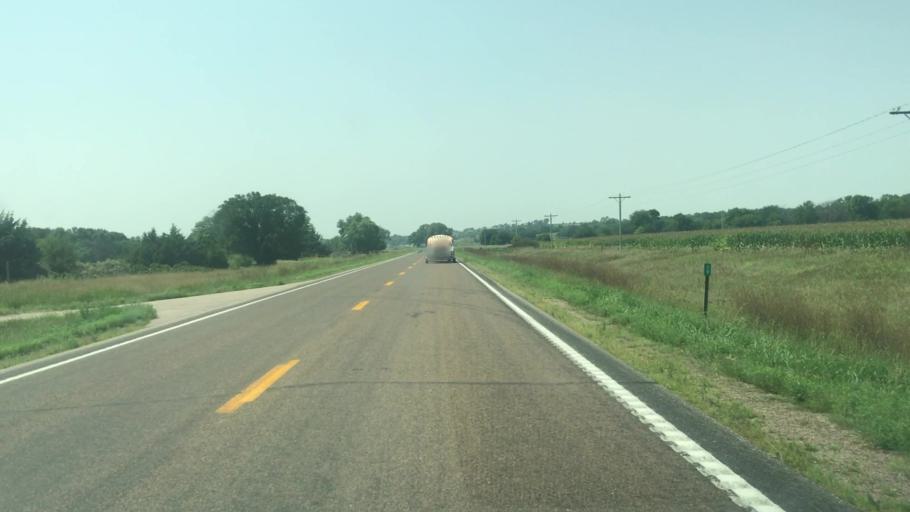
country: US
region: Nebraska
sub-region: Buffalo County
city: Ravenna
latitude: 41.0763
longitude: -98.6881
